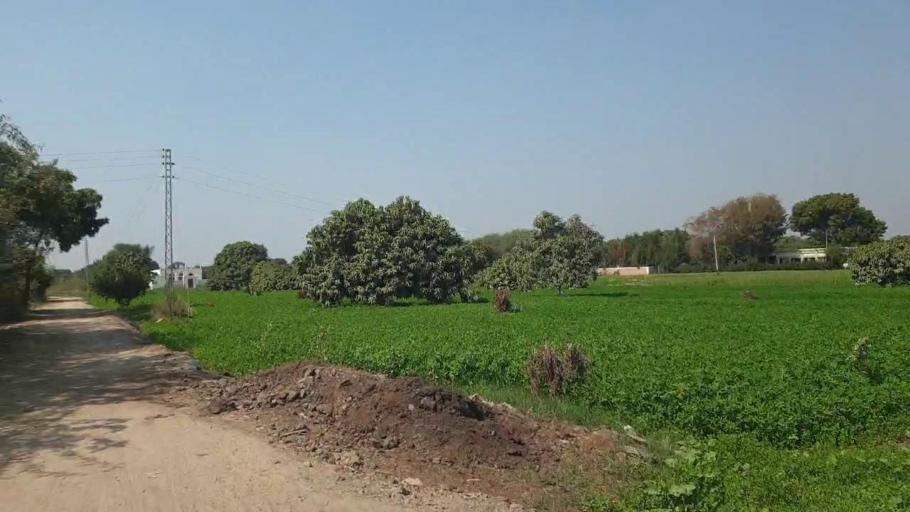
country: PK
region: Sindh
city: Chambar
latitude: 25.4061
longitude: 68.9018
